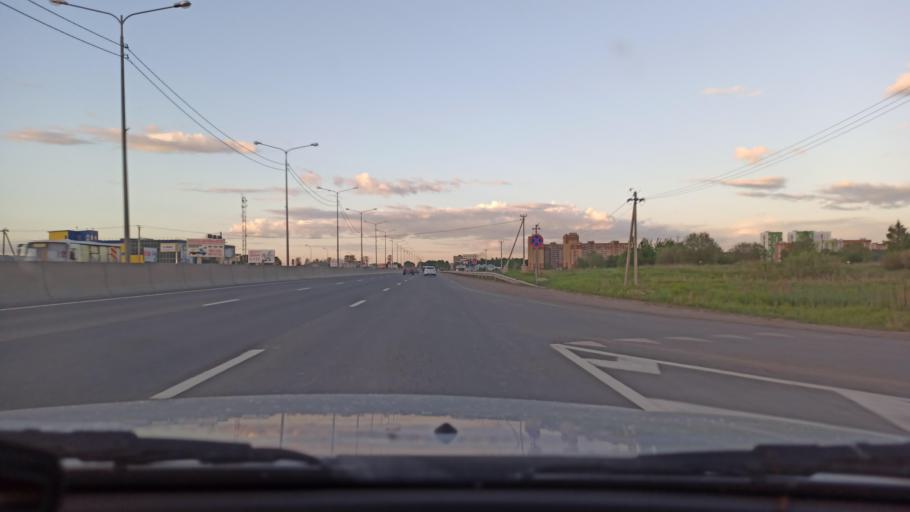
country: RU
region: Vologda
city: Vologda
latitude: 59.2144
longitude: 39.7928
